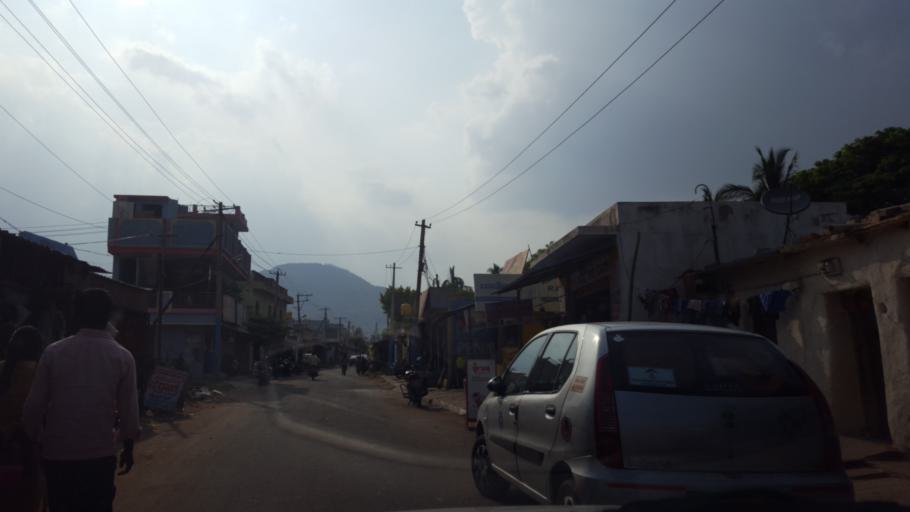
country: IN
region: Karnataka
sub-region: Chikkaballapur
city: Chik Ballapur
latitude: 13.3861
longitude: 77.7000
